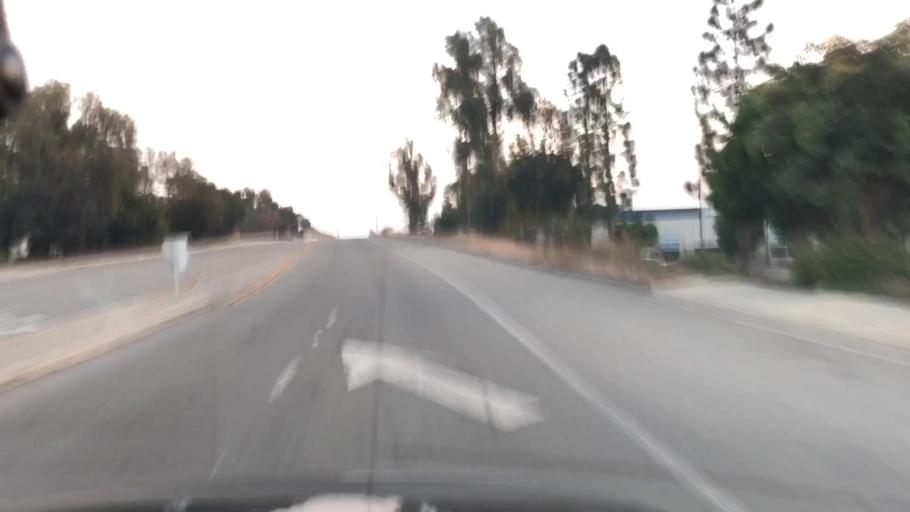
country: US
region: California
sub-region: Ventura County
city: Ventura
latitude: 34.2541
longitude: -119.2349
